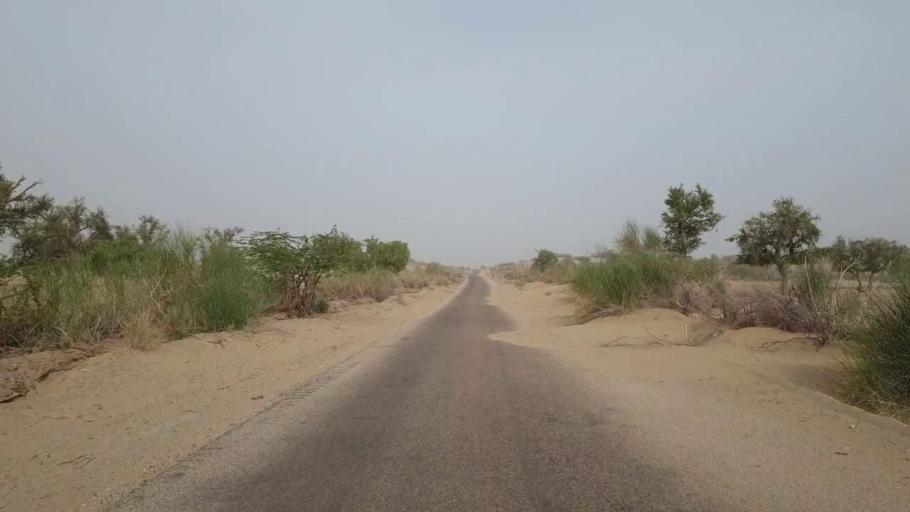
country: PK
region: Sindh
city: Islamkot
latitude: 24.5635
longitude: 70.3352
